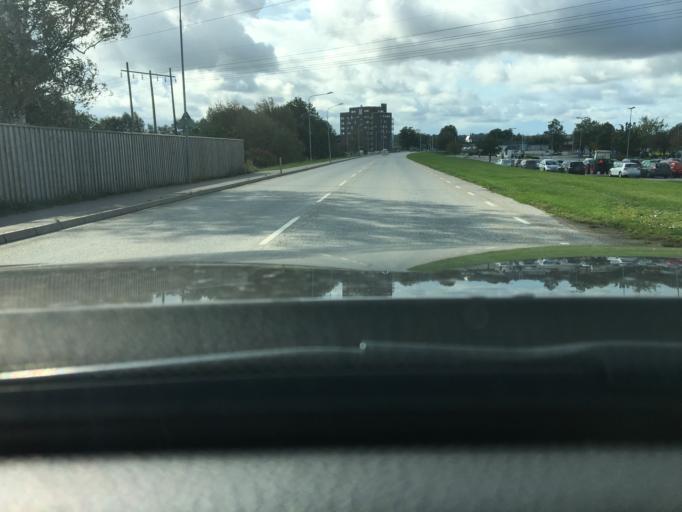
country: SE
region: Skane
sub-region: Horby Kommun
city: Hoerby
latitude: 55.8565
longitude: 13.6739
